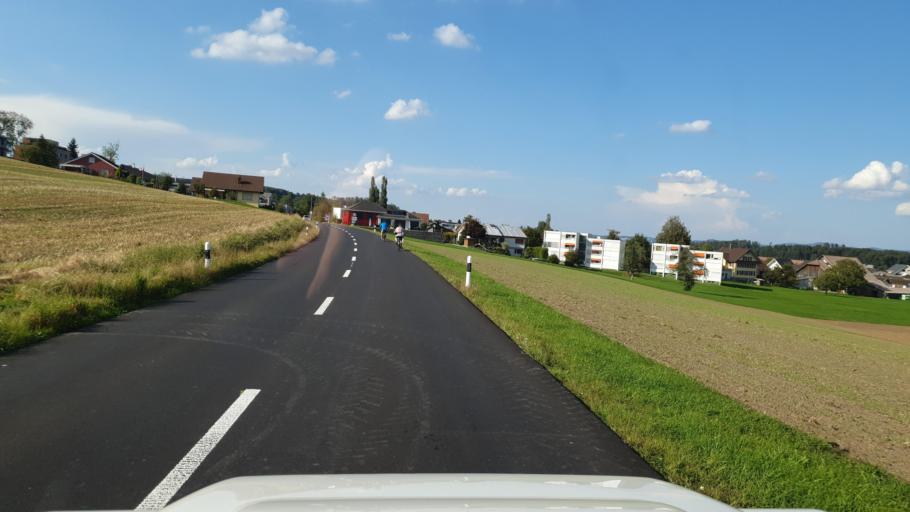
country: CH
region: Aargau
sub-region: Bezirk Muri
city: Auw
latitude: 47.2074
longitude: 8.3615
